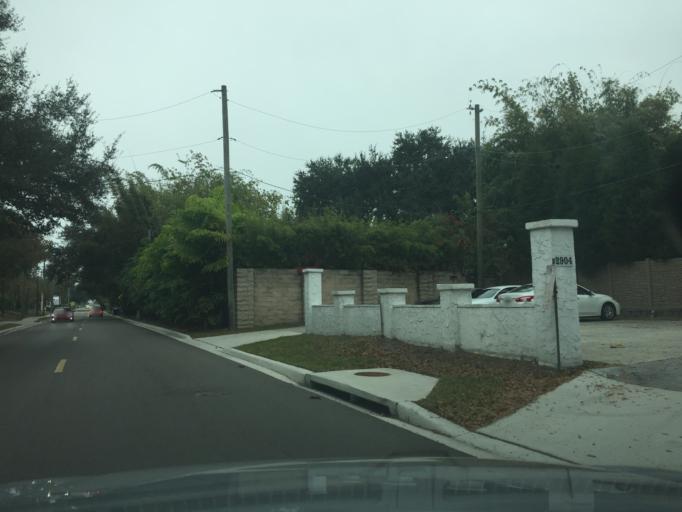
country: US
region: Florida
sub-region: Hillsborough County
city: Tampa
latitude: 27.9374
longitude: -82.4891
